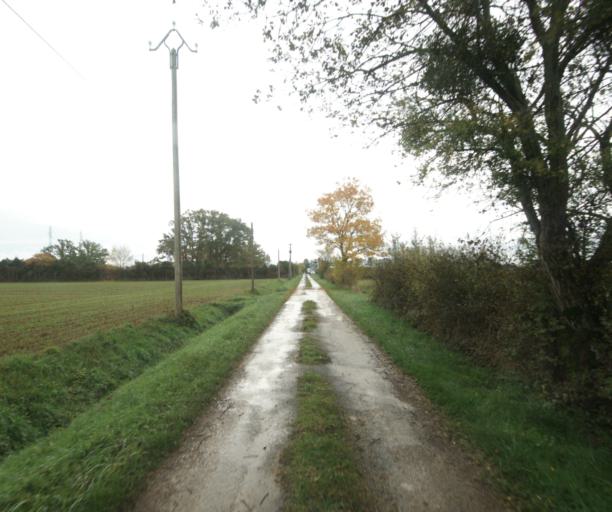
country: FR
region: Rhone-Alpes
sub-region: Departement de l'Ain
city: Pont-de-Vaux
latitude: 46.4840
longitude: 4.8831
